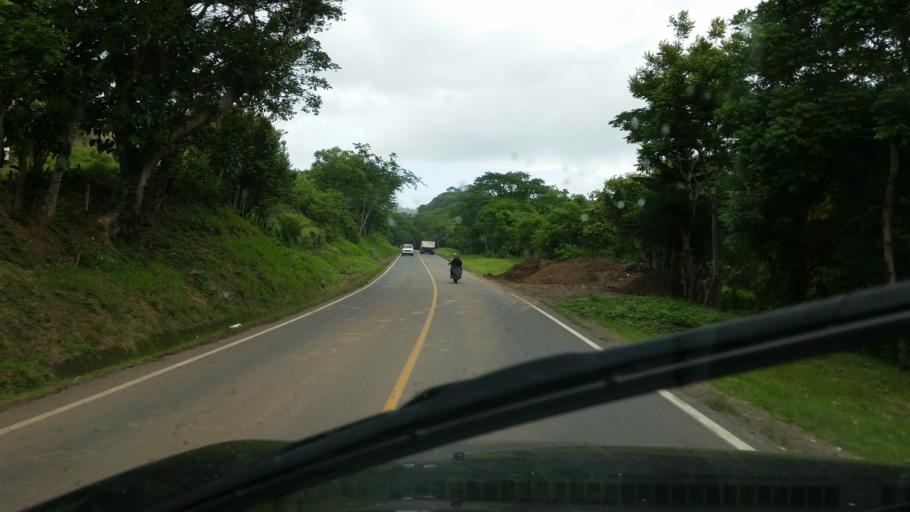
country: NI
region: Matagalpa
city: Matagalpa
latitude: 12.9404
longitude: -85.8879
